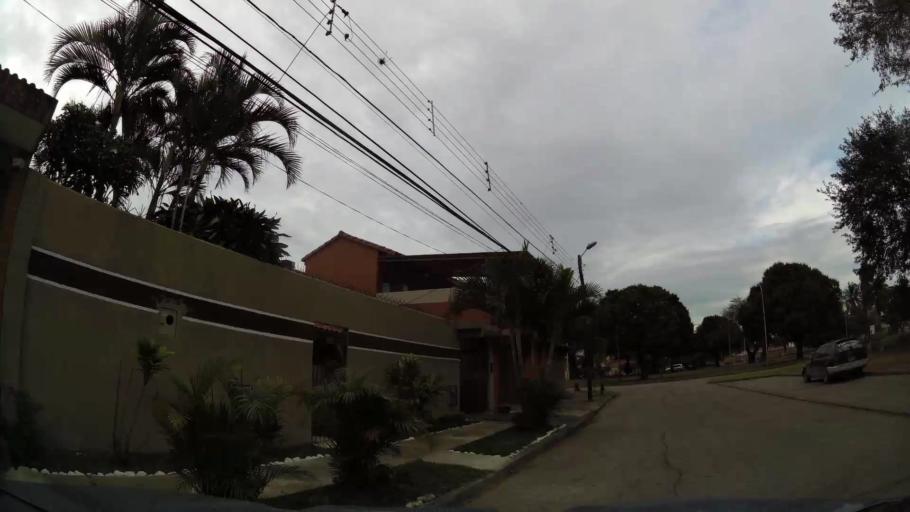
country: BO
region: Santa Cruz
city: Santa Cruz de la Sierra
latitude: -17.7669
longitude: -63.1661
